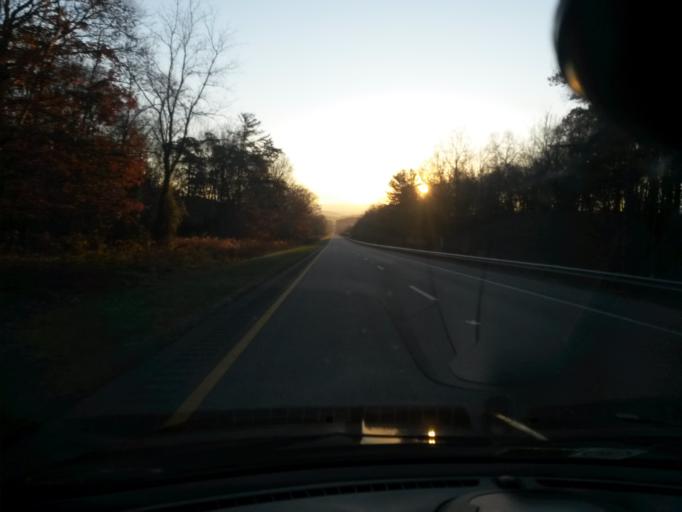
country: US
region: Virginia
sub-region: City of Lexington
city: Lexington
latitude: 37.8766
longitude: -79.5346
